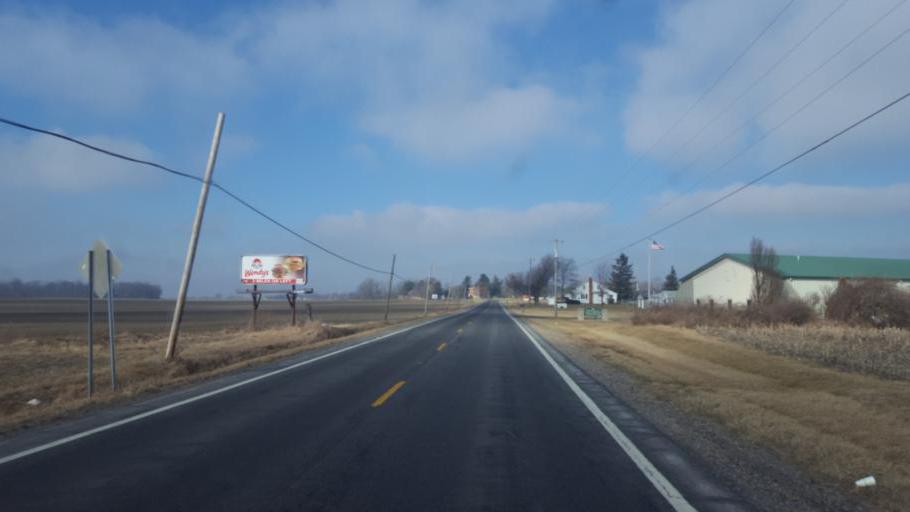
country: US
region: Ohio
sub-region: Crawford County
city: Bucyrus
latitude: 40.7811
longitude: -82.9348
